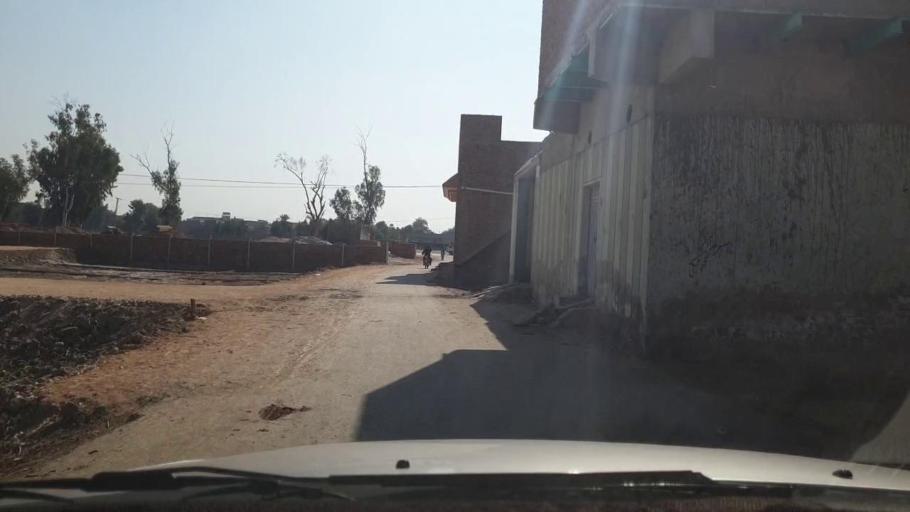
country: PK
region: Sindh
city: Mirpur Mathelo
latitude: 28.0298
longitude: 69.5512
